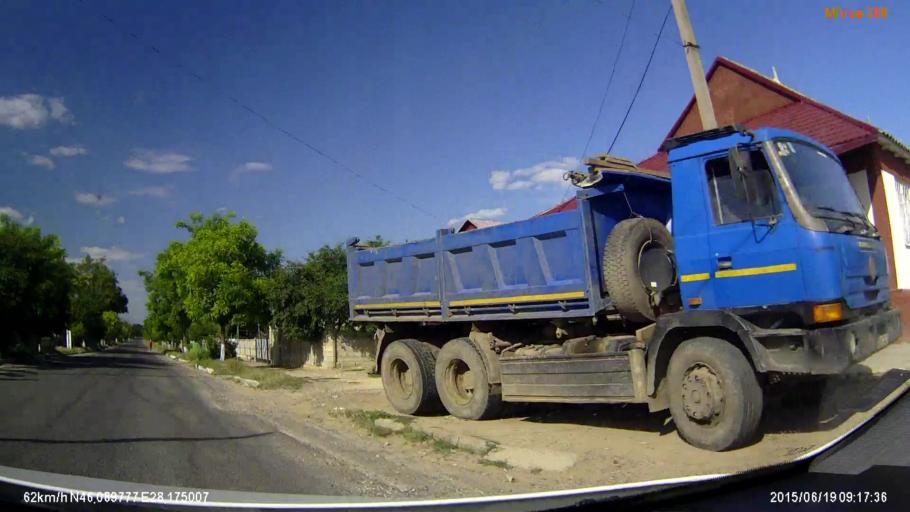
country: RO
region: Vaslui
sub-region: Oras Murgeni
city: Carja
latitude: 46.0896
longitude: 28.1749
